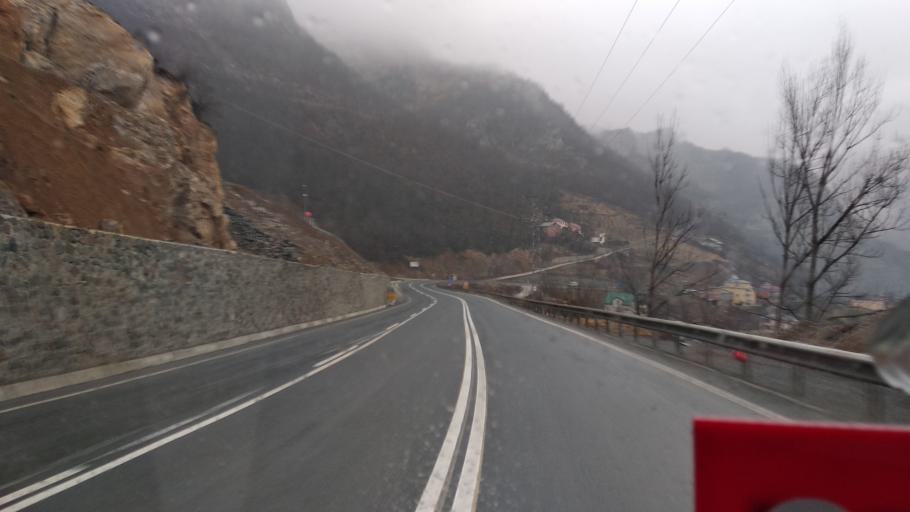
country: TR
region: Trabzon
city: Macka
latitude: 40.7152
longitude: 39.5148
